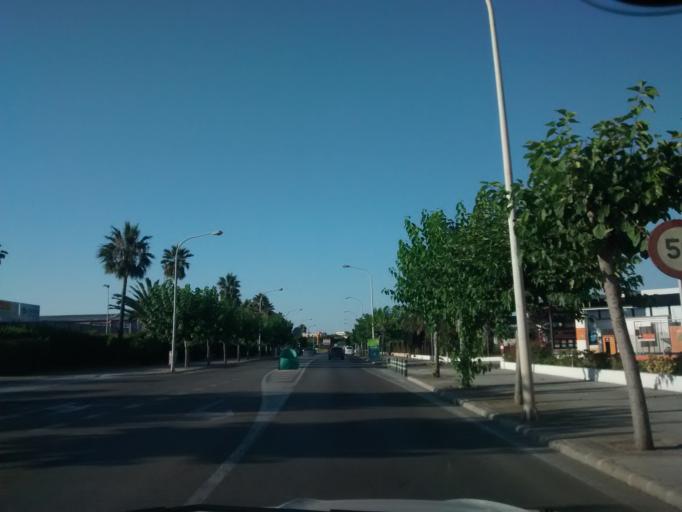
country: ES
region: Balearic Islands
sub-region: Illes Balears
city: Port d'Alcudia
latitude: 39.8405
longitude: 3.1214
